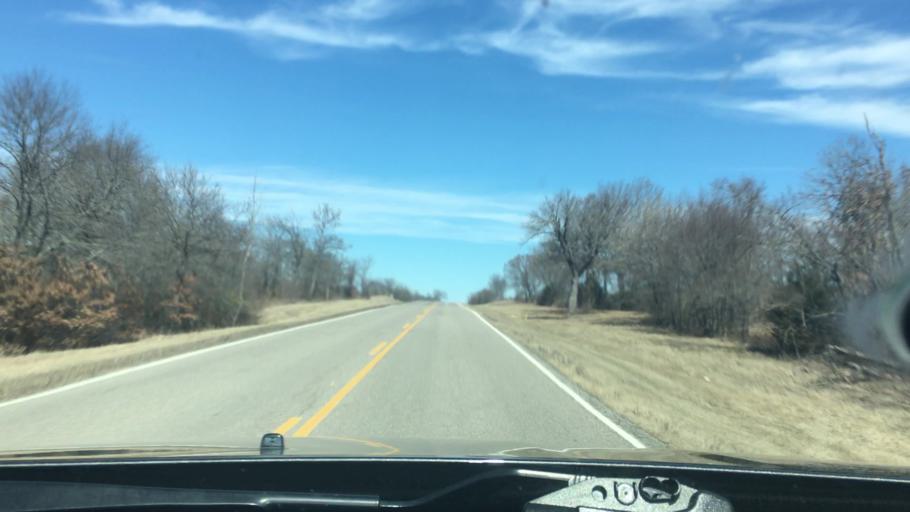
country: US
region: Oklahoma
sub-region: Carter County
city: Dickson
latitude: 34.3168
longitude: -96.9614
